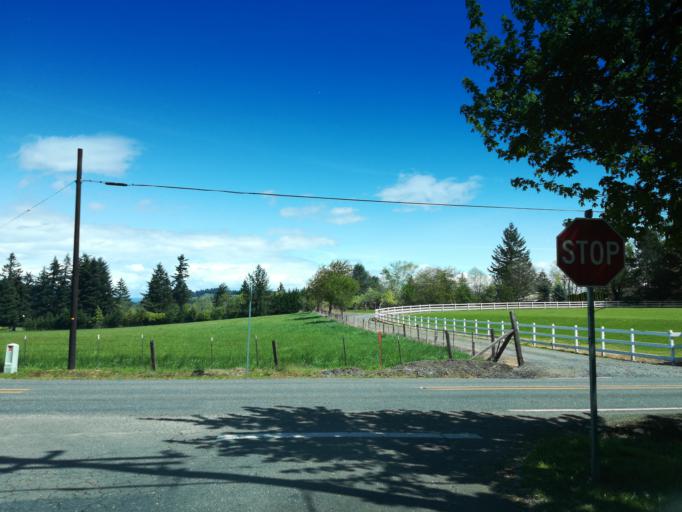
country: US
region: Oregon
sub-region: Clackamas County
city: Damascus
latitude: 45.4350
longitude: -122.4347
